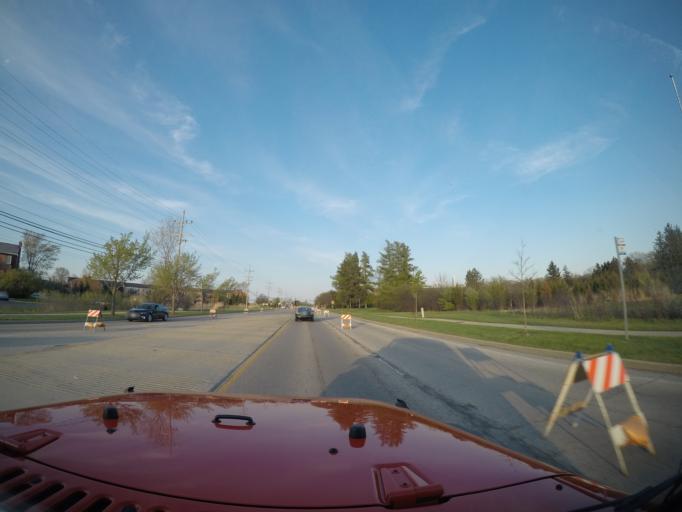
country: US
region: Illinois
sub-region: Cook County
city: Northbrook
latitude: 42.0875
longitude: -87.8620
